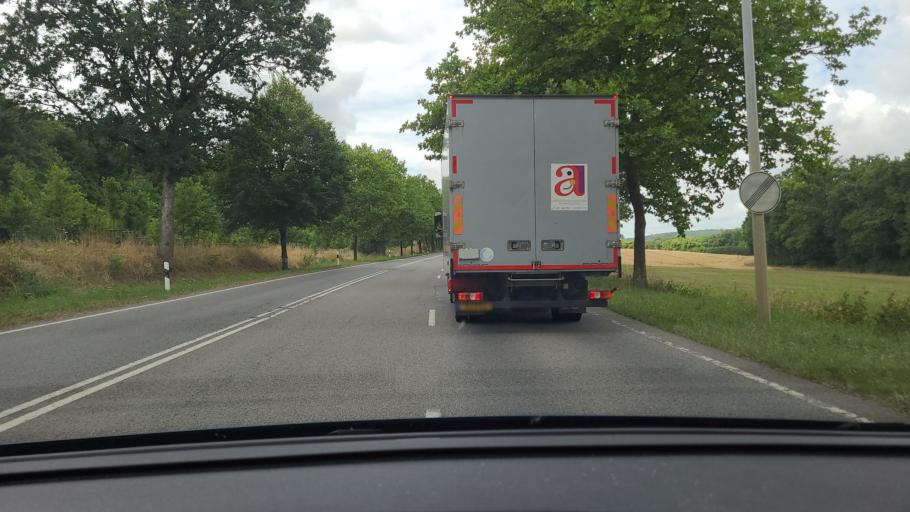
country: LU
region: Luxembourg
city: Schouweiler
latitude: 49.5741
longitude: 5.9394
